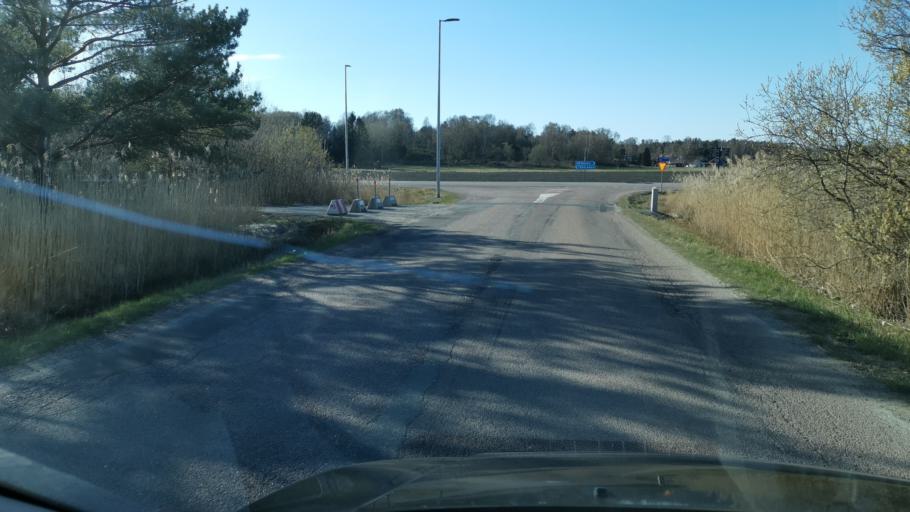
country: SE
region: Vaestra Goetaland
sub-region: Goteborg
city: Majorna
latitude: 57.7829
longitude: 11.8608
